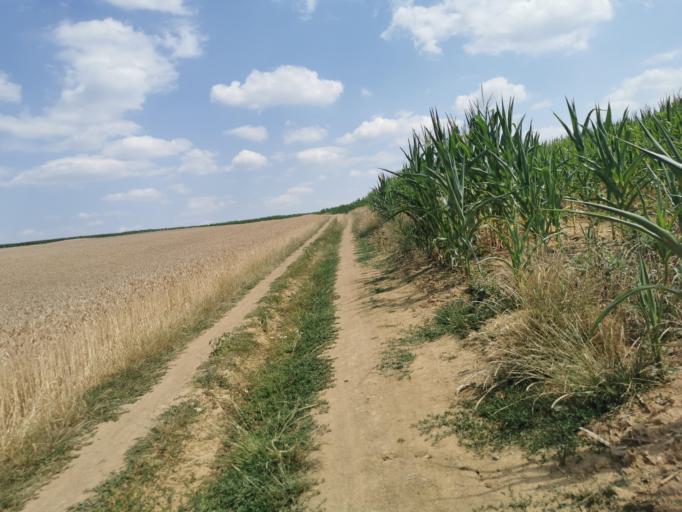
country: SK
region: Trnavsky
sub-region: Okres Senica
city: Senica
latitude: 48.6925
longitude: 17.4186
